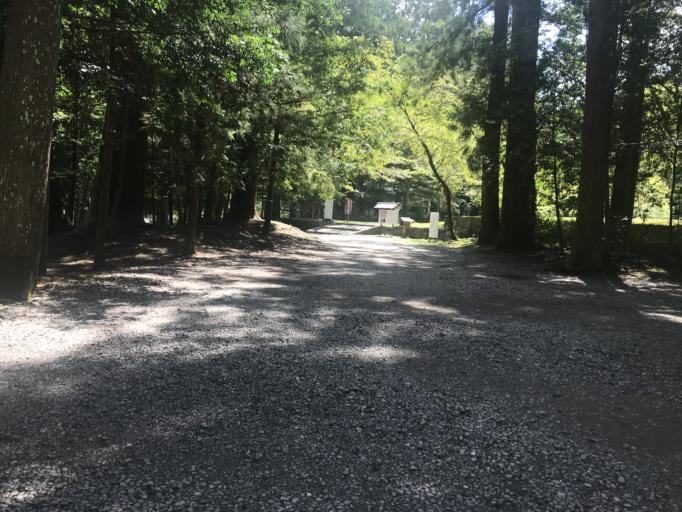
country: JP
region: Wakayama
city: Shingu
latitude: 33.8349
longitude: 135.7752
